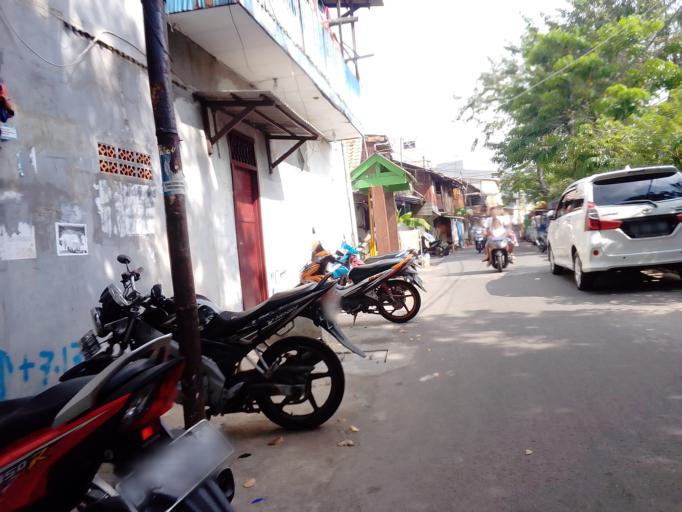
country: ID
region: Jakarta Raya
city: Jakarta
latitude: -6.1532
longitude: 106.8116
